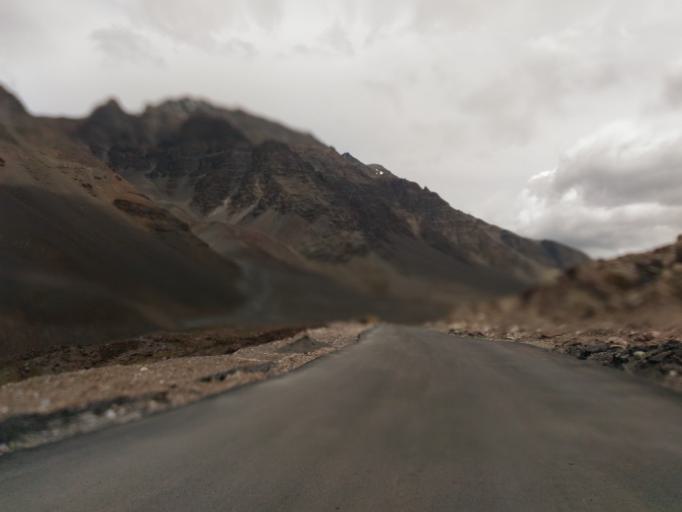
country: IN
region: Himachal Pradesh
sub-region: Lahul and Spiti
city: Kyelang
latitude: 32.7852
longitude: 77.3481
